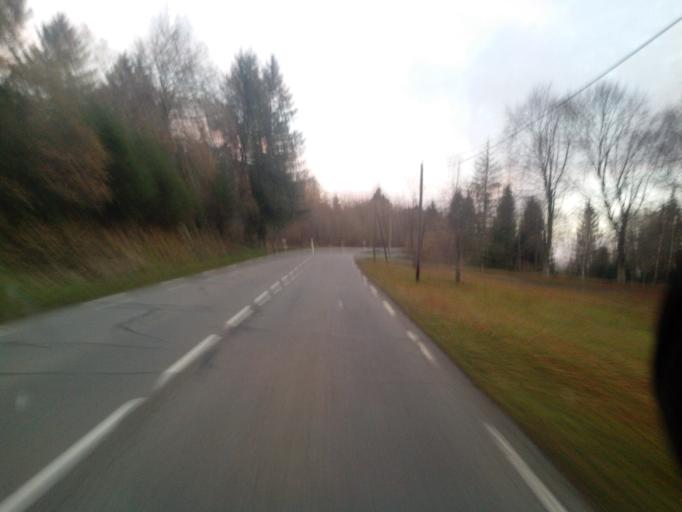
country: FR
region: Limousin
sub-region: Departement de la Correze
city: Meymac
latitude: 45.5235
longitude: 2.1631
